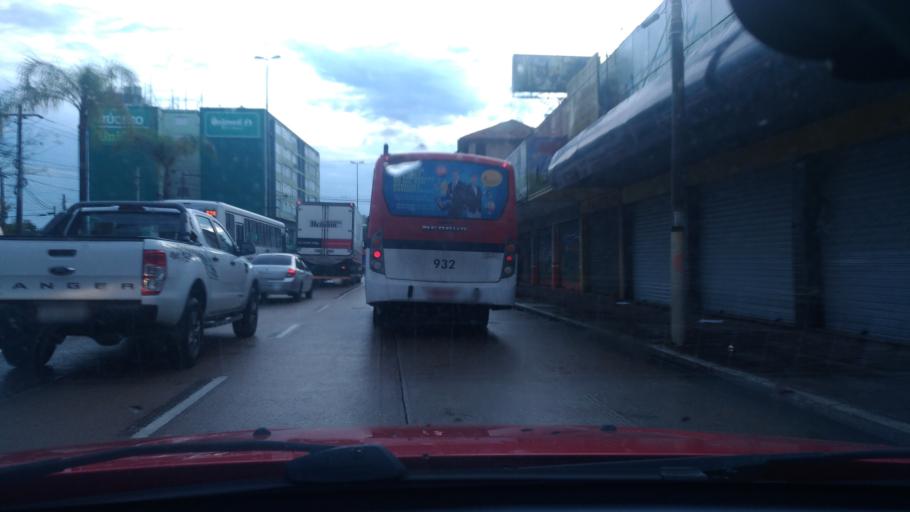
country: BR
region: Rio Grande do Sul
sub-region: Porto Alegre
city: Porto Alegre
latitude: -30.0179
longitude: -51.2088
